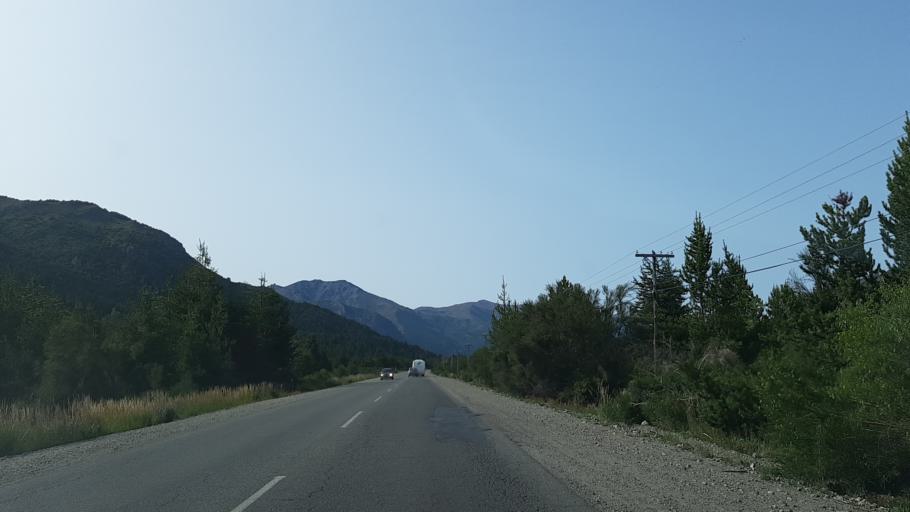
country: AR
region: Rio Negro
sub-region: Departamento de Bariloche
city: San Carlos de Bariloche
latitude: -41.1370
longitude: -71.4124
